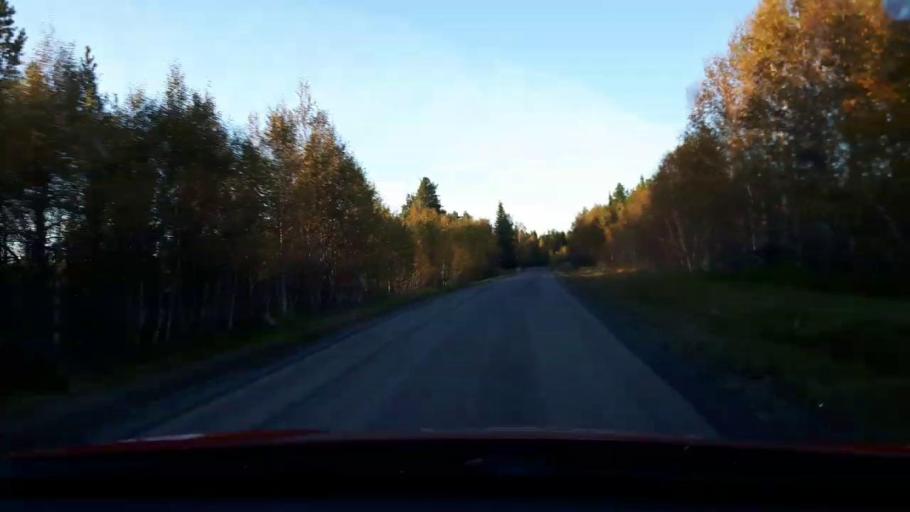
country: SE
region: Jaemtland
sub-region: Krokoms Kommun
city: Krokom
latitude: 63.4384
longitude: 14.4214
